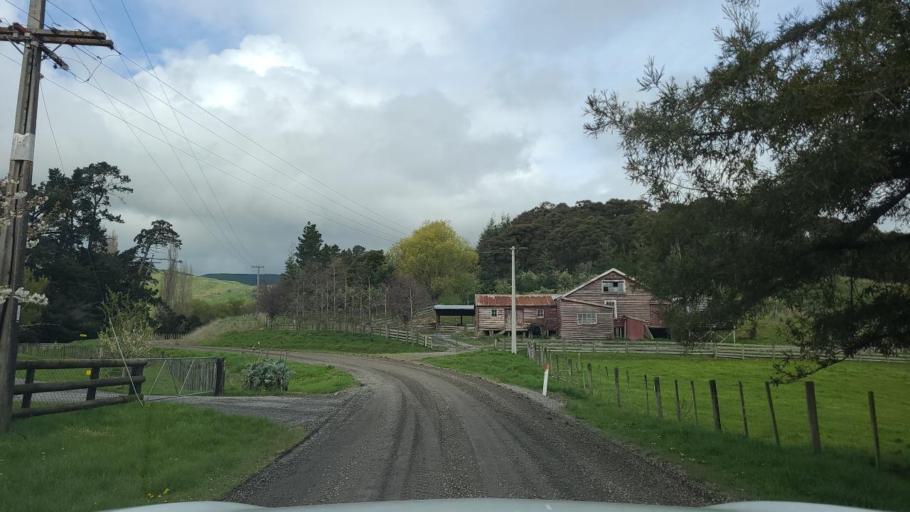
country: NZ
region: Wellington
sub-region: Masterton District
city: Masterton
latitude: -41.1560
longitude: 175.6084
